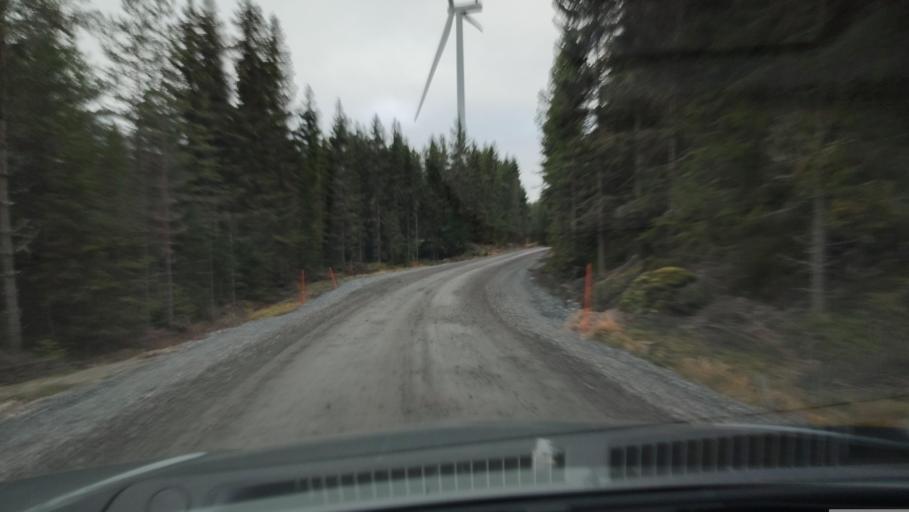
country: FI
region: Ostrobothnia
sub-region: Sydosterbotten
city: Kristinestad
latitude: 62.1937
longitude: 21.5446
